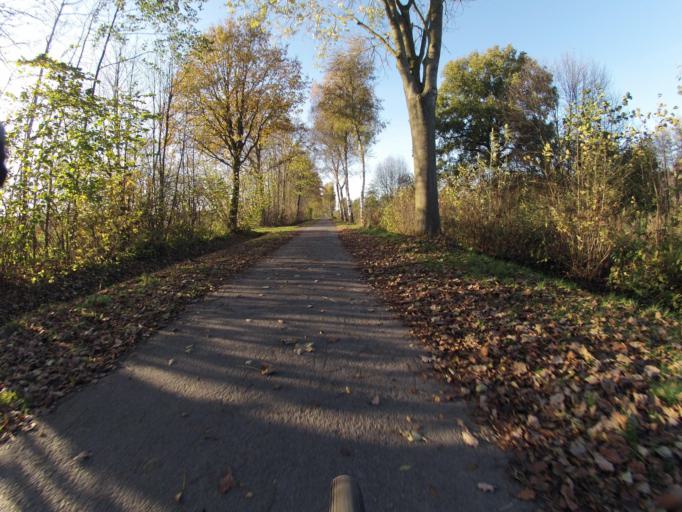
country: DE
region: North Rhine-Westphalia
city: Ibbenburen
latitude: 52.2793
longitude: 7.6931
